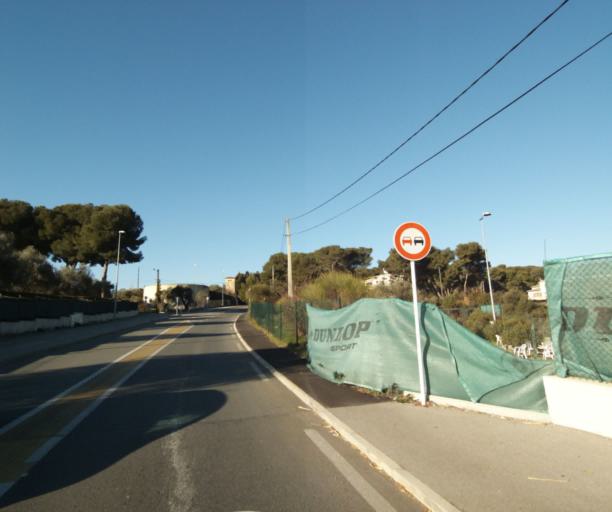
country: FR
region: Provence-Alpes-Cote d'Azur
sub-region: Departement des Alpes-Maritimes
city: Biot
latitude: 43.5960
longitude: 7.0836
